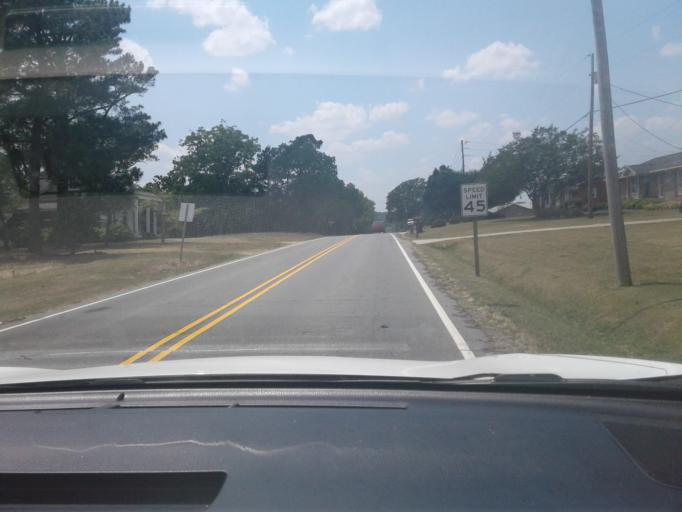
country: US
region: North Carolina
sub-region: Johnston County
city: Benson
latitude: 35.3880
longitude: -78.5661
